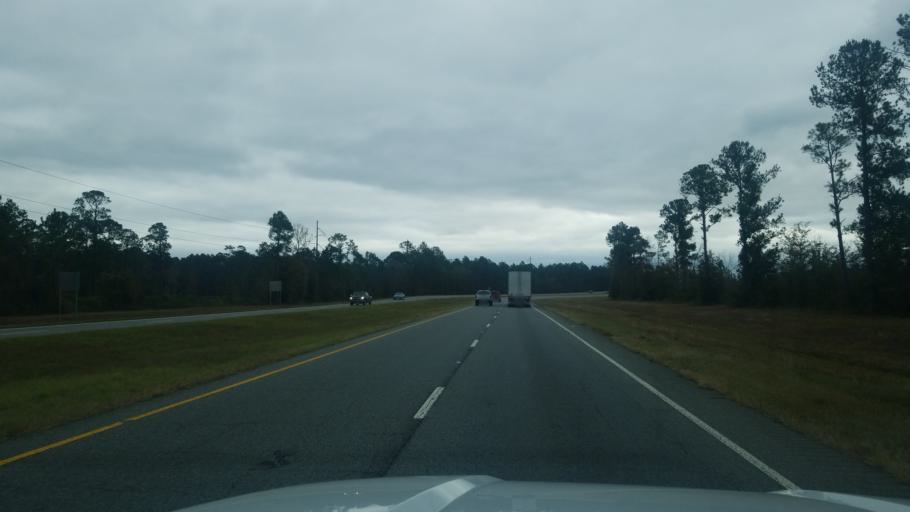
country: US
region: Georgia
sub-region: Ware County
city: Deenwood
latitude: 31.2409
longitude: -82.4293
